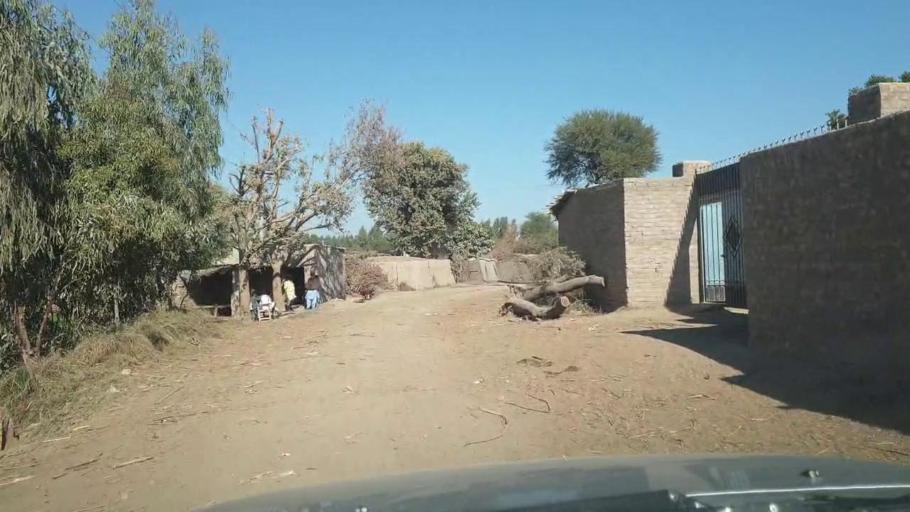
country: PK
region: Sindh
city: Ghotki
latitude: 28.1010
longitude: 69.3419
